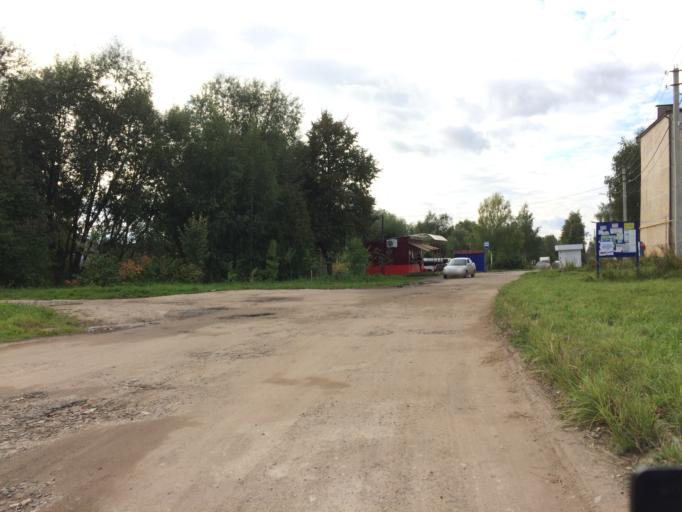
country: RU
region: Mariy-El
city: Yoshkar-Ola
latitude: 56.6553
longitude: 48.0098
